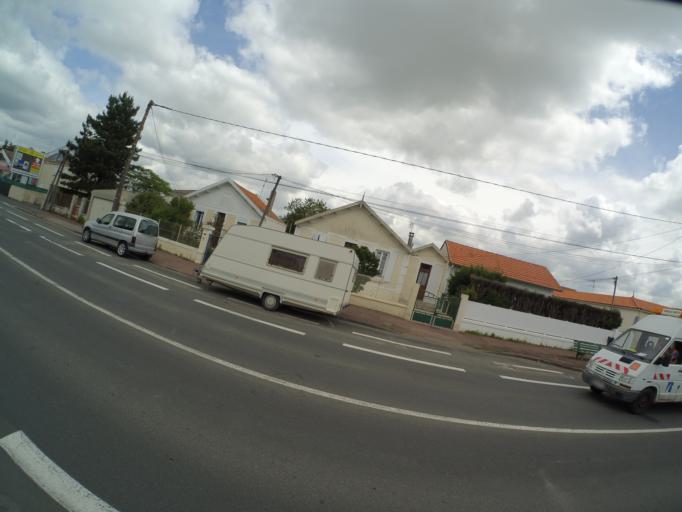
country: FR
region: Poitou-Charentes
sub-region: Departement de la Charente-Maritime
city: Rochefort
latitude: 45.9291
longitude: -0.9600
